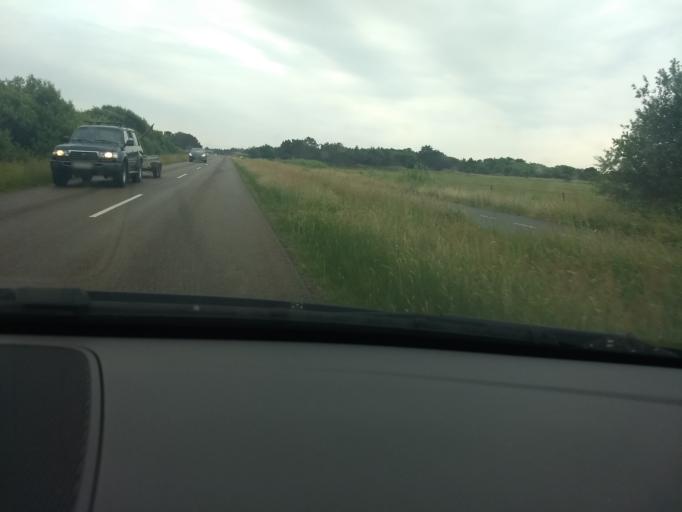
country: DK
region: South Denmark
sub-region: Fano Kommune
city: Nordby
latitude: 55.3644
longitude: 8.4570
